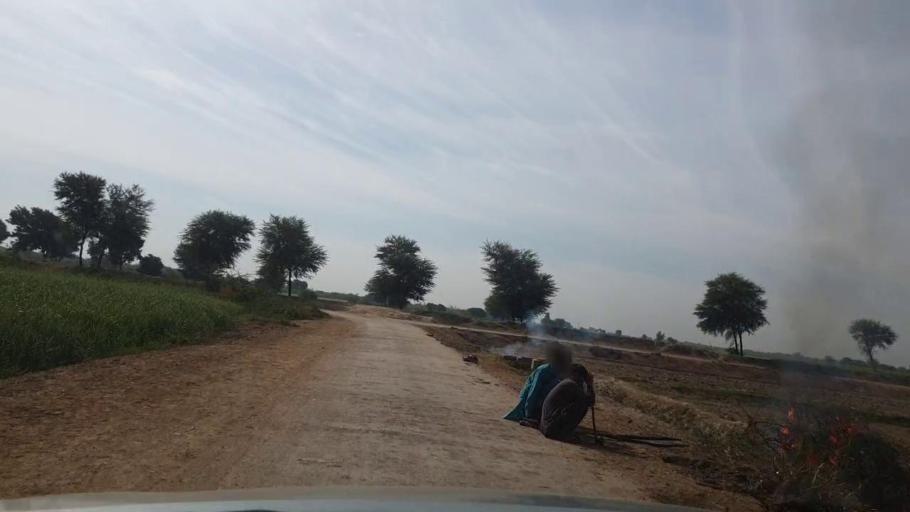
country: PK
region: Sindh
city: Kunri
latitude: 25.1517
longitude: 69.6023
